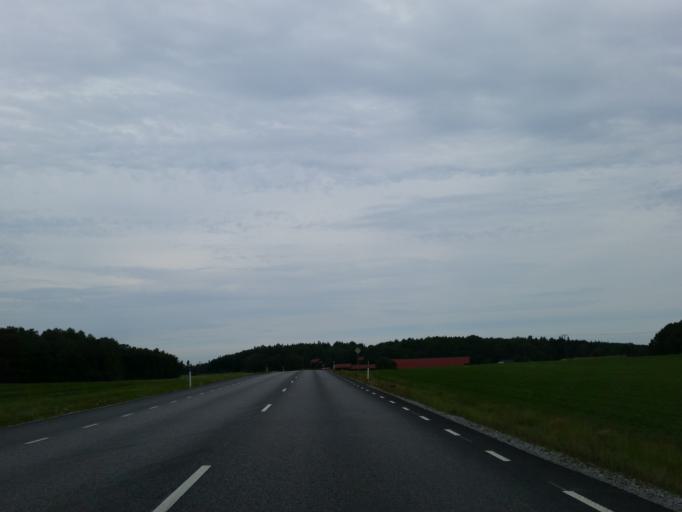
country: SE
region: Stockholm
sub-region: Salems Kommun
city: Ronninge
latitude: 59.2179
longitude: 17.7608
